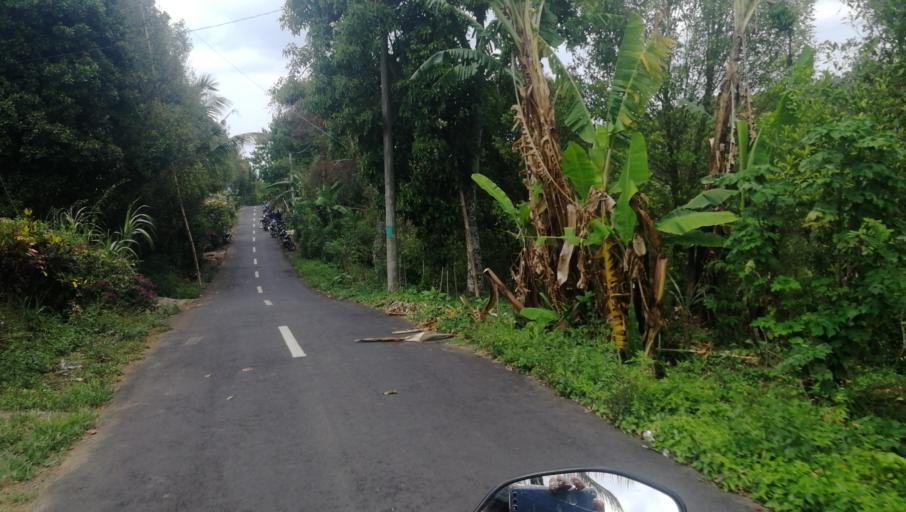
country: ID
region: Bali
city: Munduk
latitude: -8.3006
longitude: 115.0560
